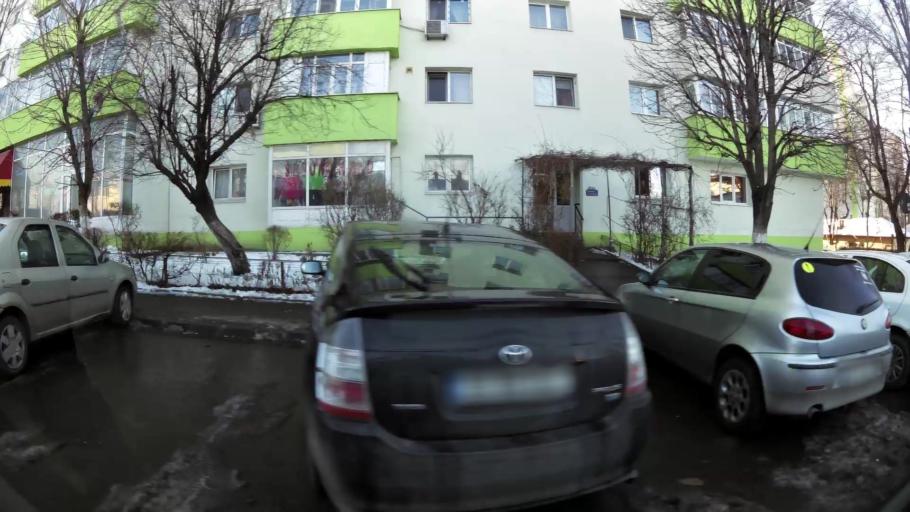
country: RO
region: Ilfov
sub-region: Comuna Fundeni-Dobroesti
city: Fundeni
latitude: 44.4694
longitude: 26.1424
